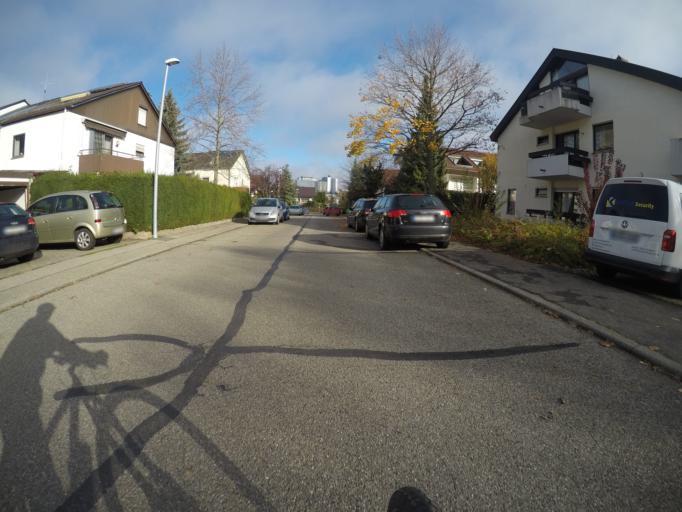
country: DE
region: Baden-Wuerttemberg
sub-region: Regierungsbezirk Stuttgart
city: Leinfelden-Echterdingen
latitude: 48.7197
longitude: 9.1515
